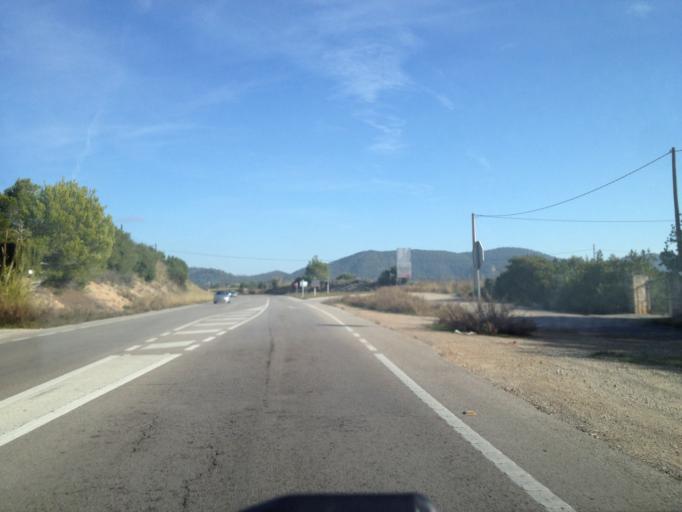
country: ES
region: Balearic Islands
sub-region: Illes Balears
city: Son Servera
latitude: 39.6370
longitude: 3.3681
